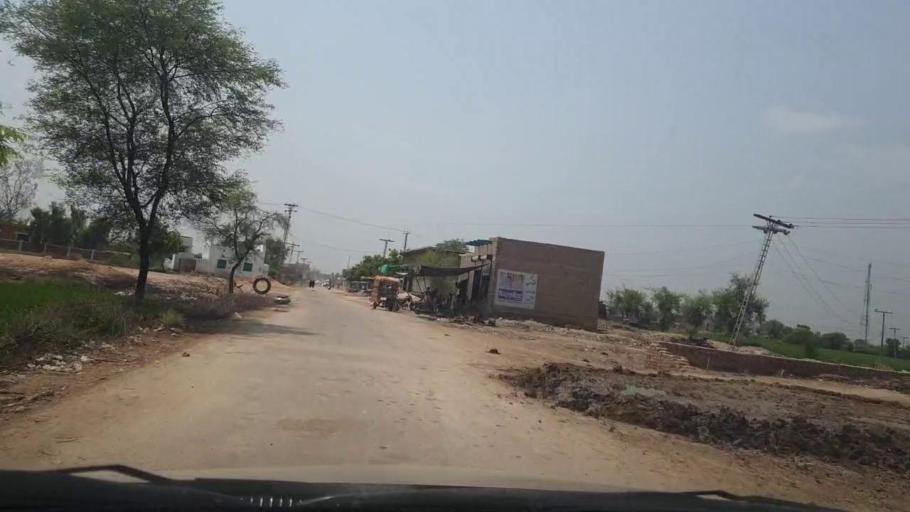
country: PK
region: Sindh
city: Ratodero
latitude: 27.7307
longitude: 68.2840
